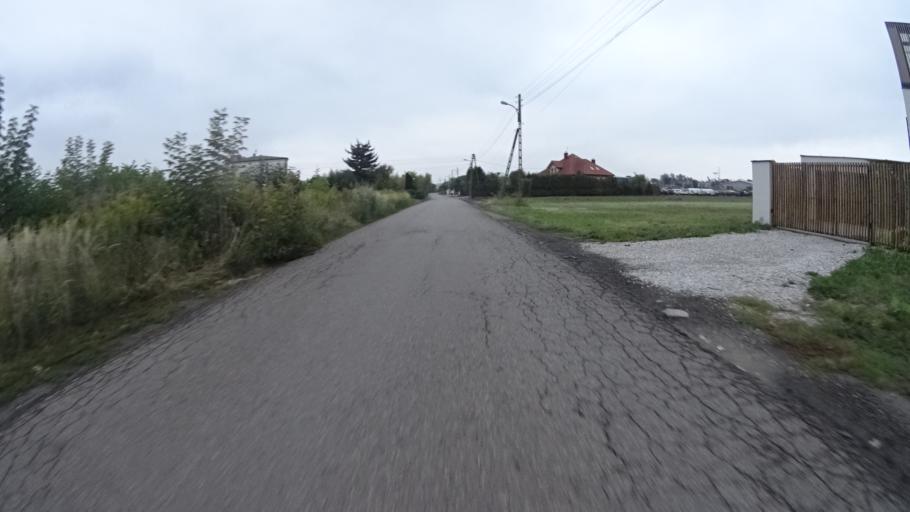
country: PL
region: Masovian Voivodeship
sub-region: Warszawa
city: Ursus
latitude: 52.2197
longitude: 20.8826
